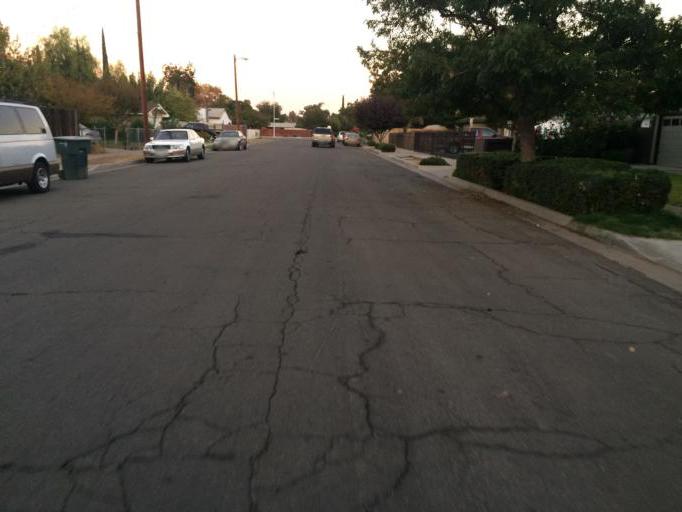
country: US
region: California
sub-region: Fresno County
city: Fresno
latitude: 36.7468
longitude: -119.7377
